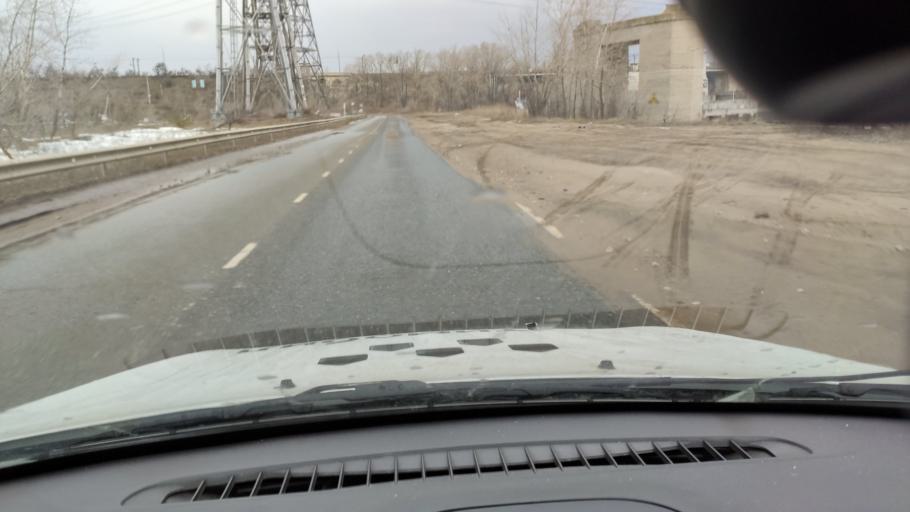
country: RU
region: Samara
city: Zhigulevsk
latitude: 53.4623
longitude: 49.5070
